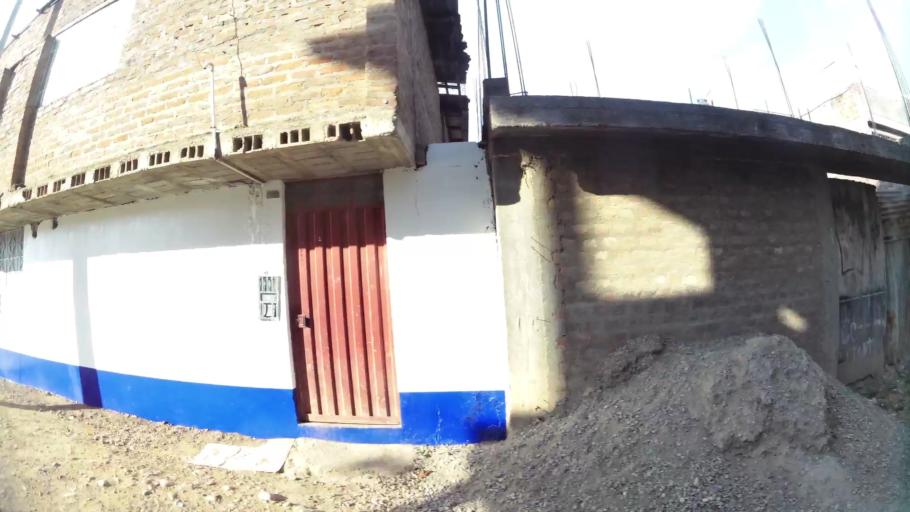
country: PE
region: Junin
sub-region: Provincia de Huancayo
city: El Tambo
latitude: -12.0480
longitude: -75.2169
